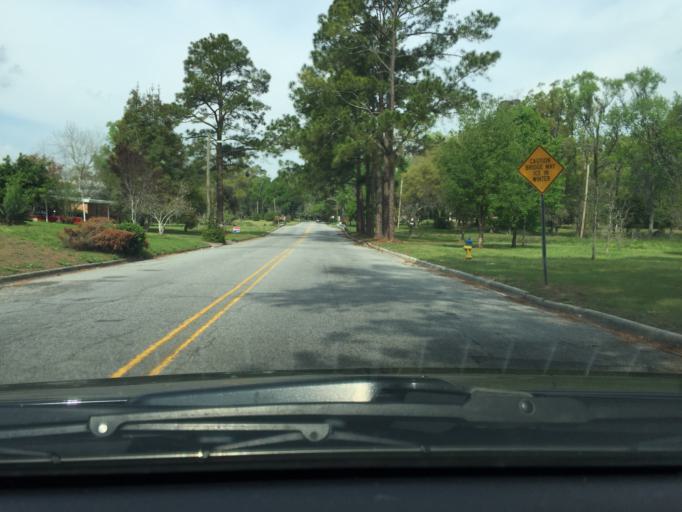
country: US
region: Georgia
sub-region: Chatham County
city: Montgomery
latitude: 31.9840
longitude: -81.1340
